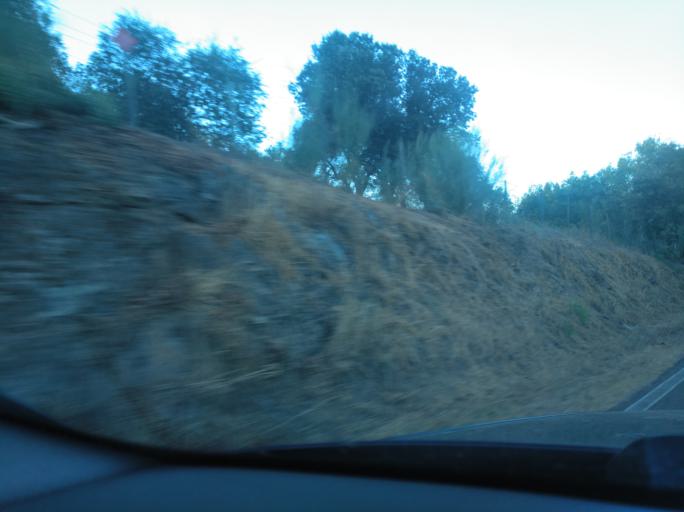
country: PT
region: Portalegre
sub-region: Arronches
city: Arronches
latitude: 39.0693
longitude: -7.2517
